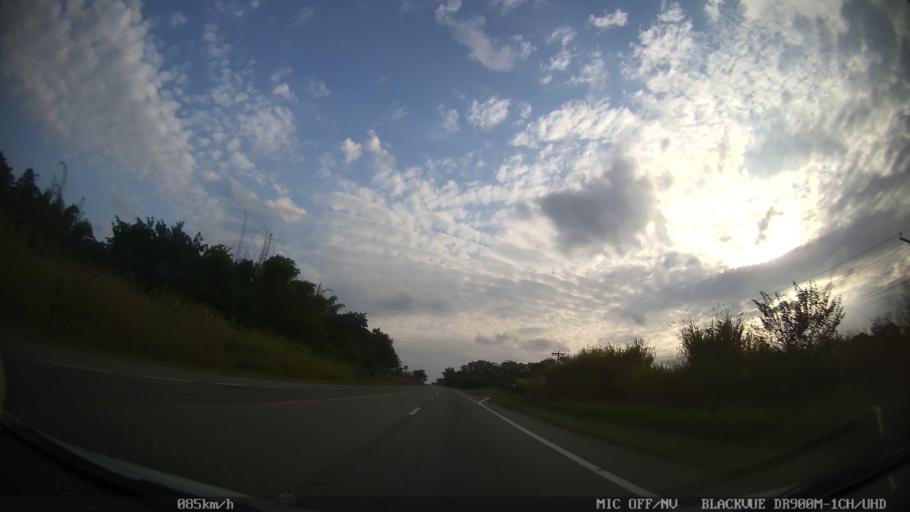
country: BR
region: Sao Paulo
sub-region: Cosmopolis
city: Cosmopolis
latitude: -22.6320
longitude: -47.3004
